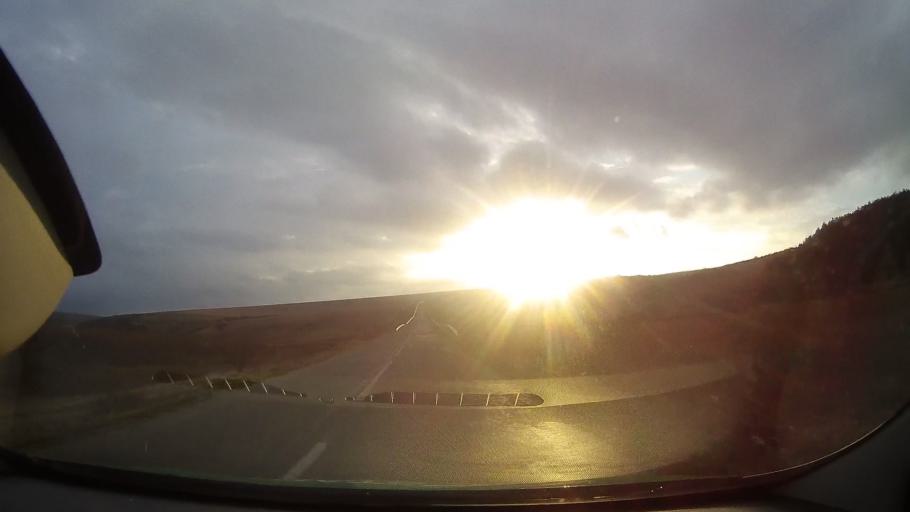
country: RO
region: Constanta
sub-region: Comuna Adamclisi
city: Adamclisi
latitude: 44.0388
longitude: 27.9418
